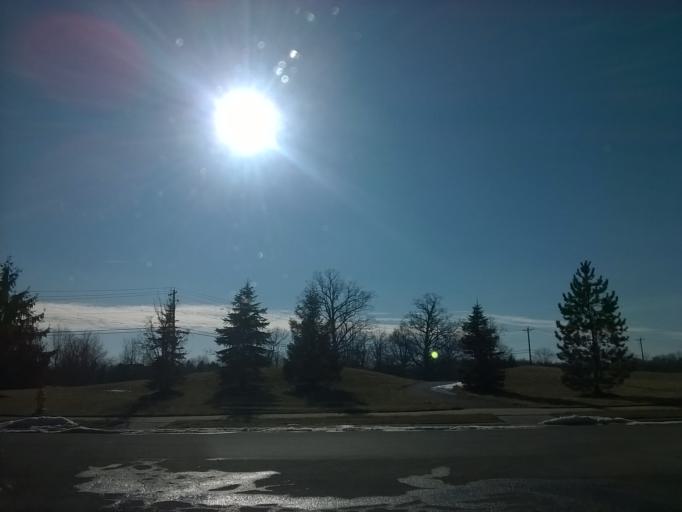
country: US
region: Indiana
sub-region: Boone County
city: Zionsville
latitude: 39.9781
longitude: -86.2090
